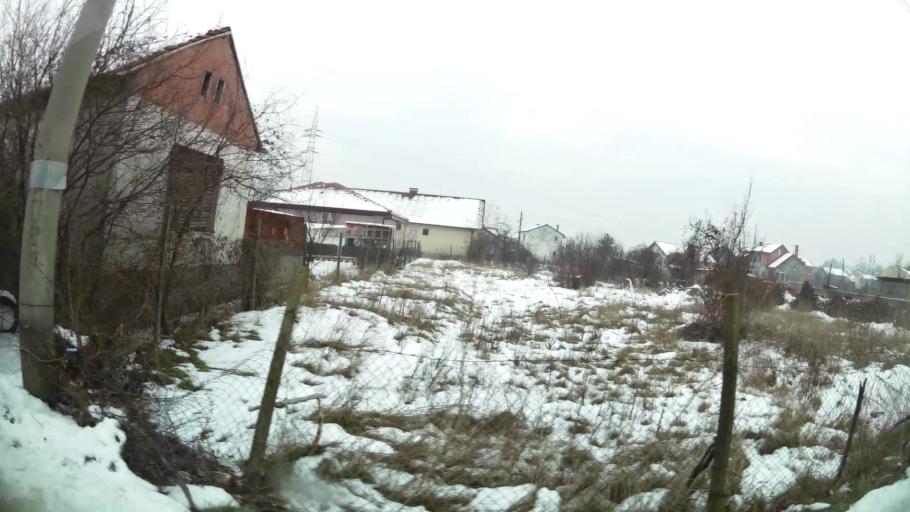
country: MK
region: Saraj
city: Saraj
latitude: 42.0401
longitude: 21.3512
